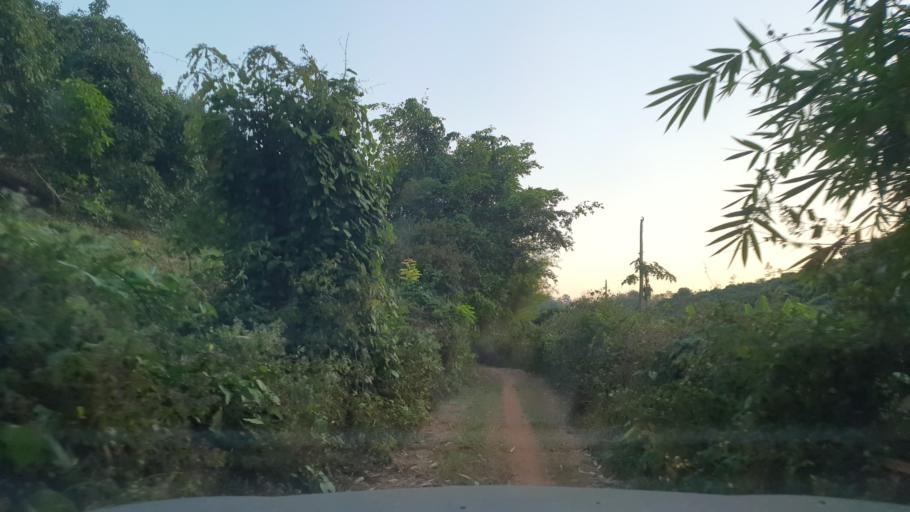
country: TH
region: Chiang Mai
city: Mae Wang
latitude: 18.6961
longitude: 98.8151
